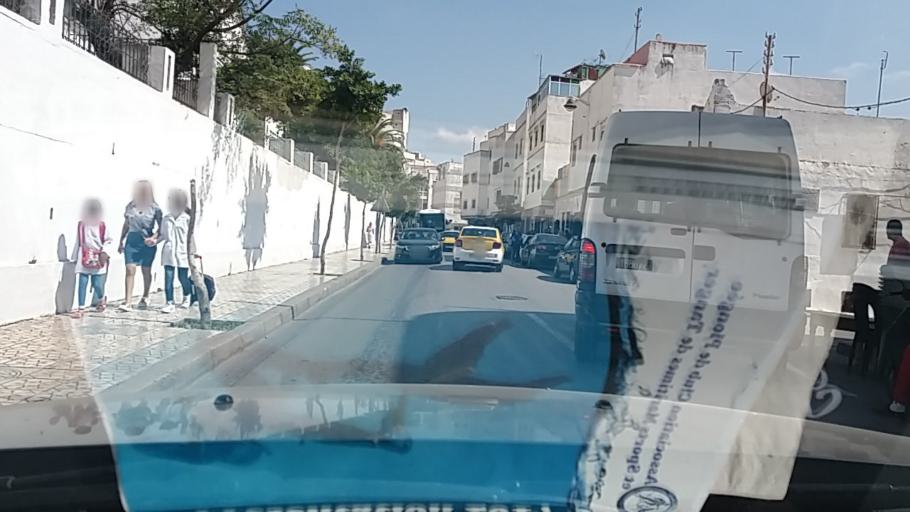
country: MA
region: Tanger-Tetouan
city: Tetouan
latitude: 35.5746
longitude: -5.3808
